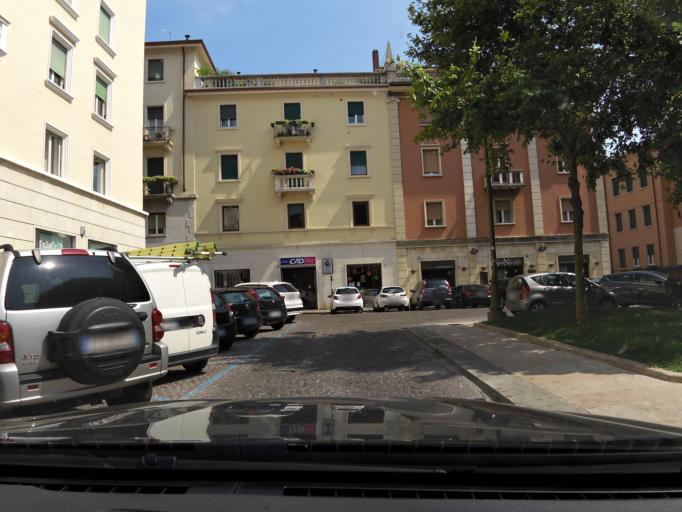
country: IT
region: Veneto
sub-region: Provincia di Verona
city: Verona
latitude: 45.4400
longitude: 10.9959
